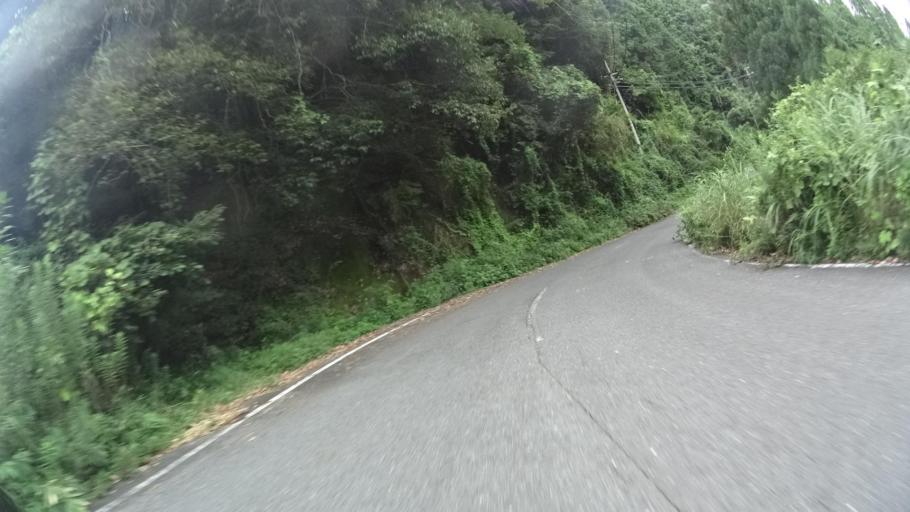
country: JP
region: Mie
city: Nabari
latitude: 34.7146
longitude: 136.0067
